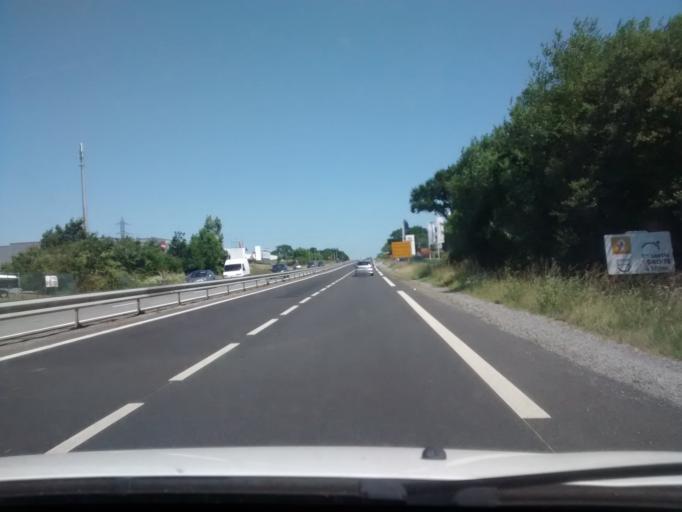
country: FR
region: Brittany
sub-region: Departement d'Ille-et-Vilaine
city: La Richardais
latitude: 48.6132
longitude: -2.0506
